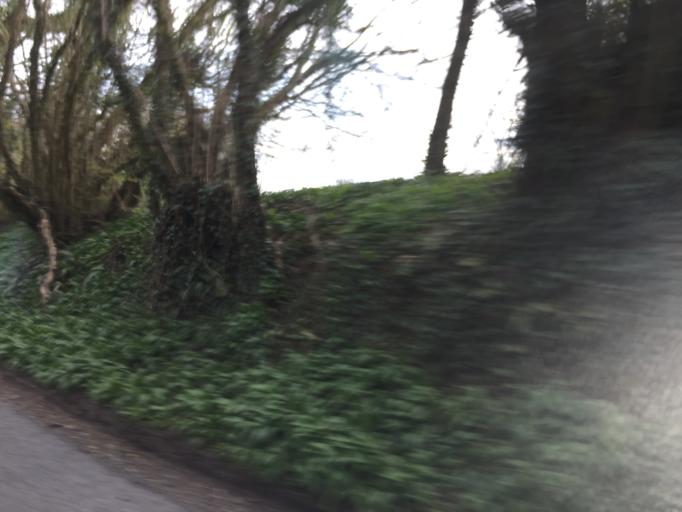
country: GB
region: Wales
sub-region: Caerphilly County Borough
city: Caerphilly
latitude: 51.5510
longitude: -3.2371
